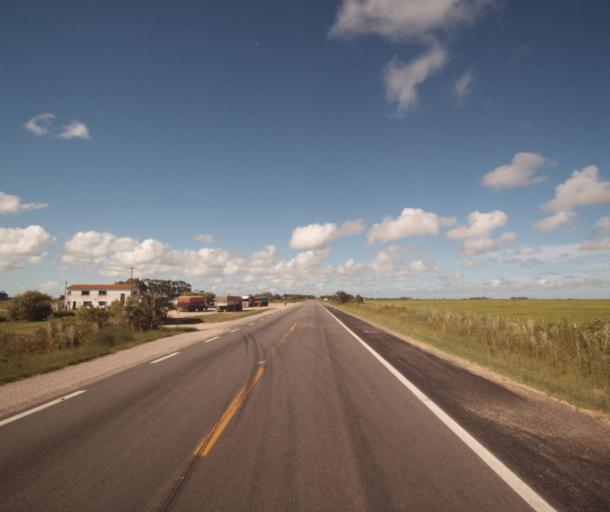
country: UY
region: Cerro Largo
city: Rio Branco
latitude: -33.0433
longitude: -52.8644
